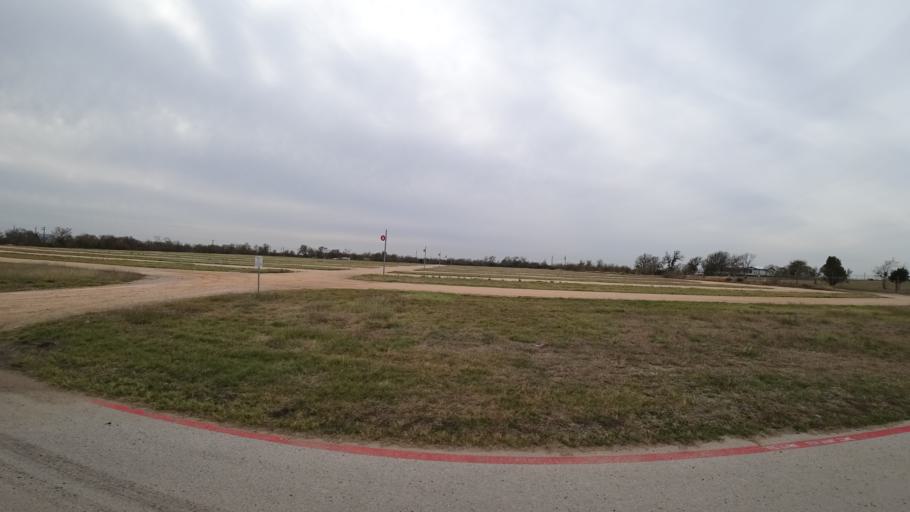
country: US
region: Texas
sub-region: Travis County
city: Garfield
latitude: 30.1375
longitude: -97.6209
